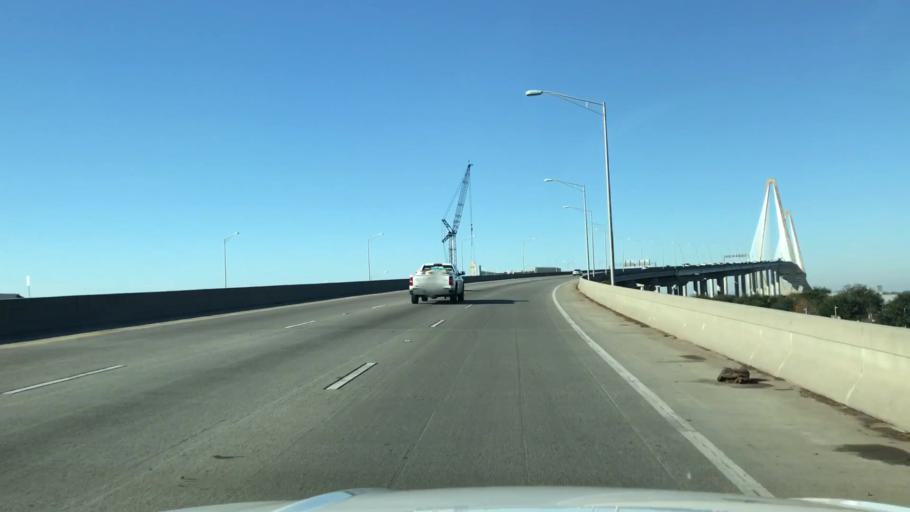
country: US
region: South Carolina
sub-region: Charleston County
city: Mount Pleasant
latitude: 32.8014
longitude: -79.8993
